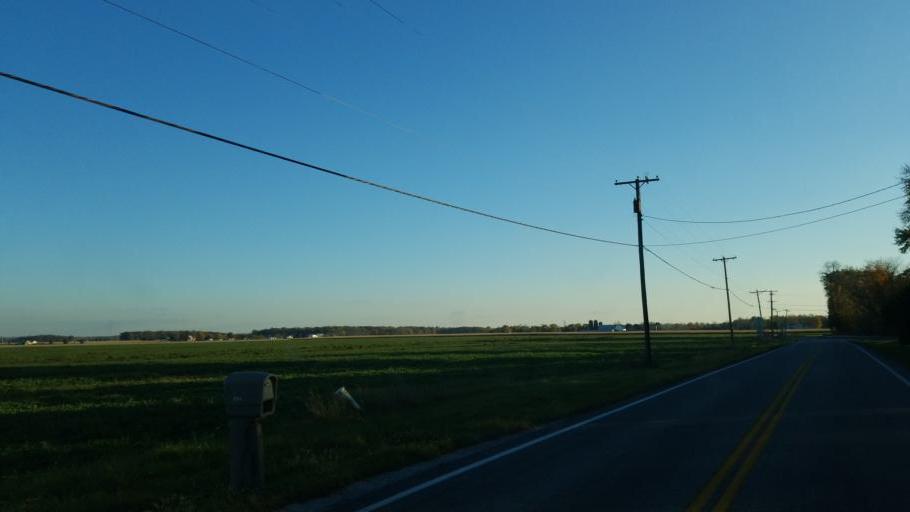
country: US
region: Ohio
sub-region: Sandusky County
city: Green Springs
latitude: 41.3208
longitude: -83.0567
